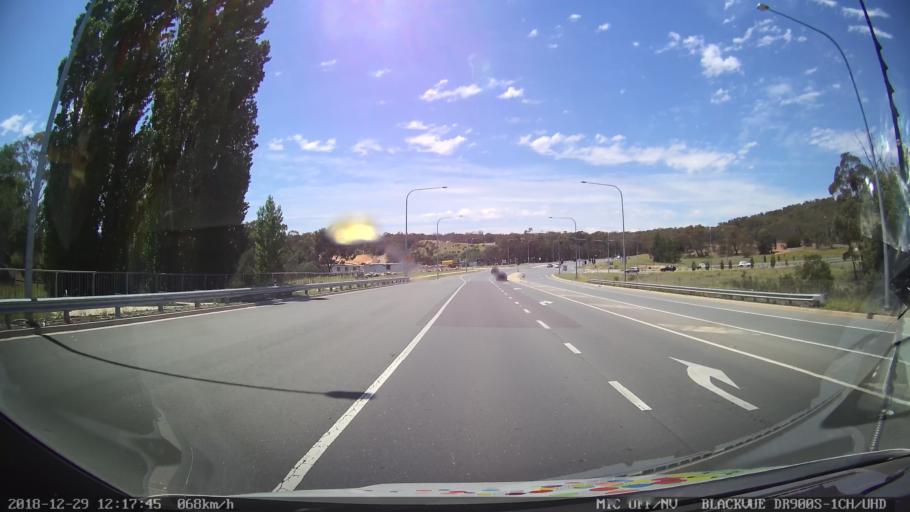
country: AU
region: New South Wales
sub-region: Queanbeyan
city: Queanbeyan
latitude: -35.3779
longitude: 149.2349
